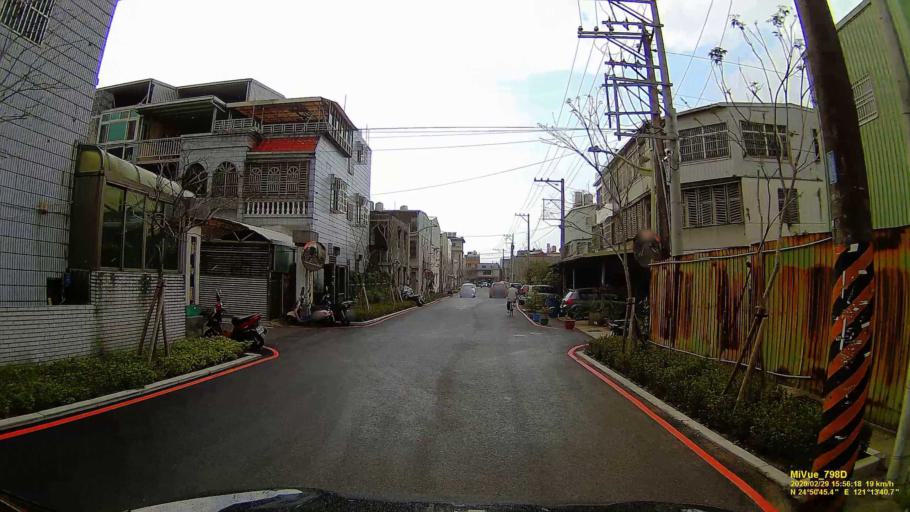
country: TW
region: Taiwan
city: Daxi
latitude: 24.8460
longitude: 121.2279
